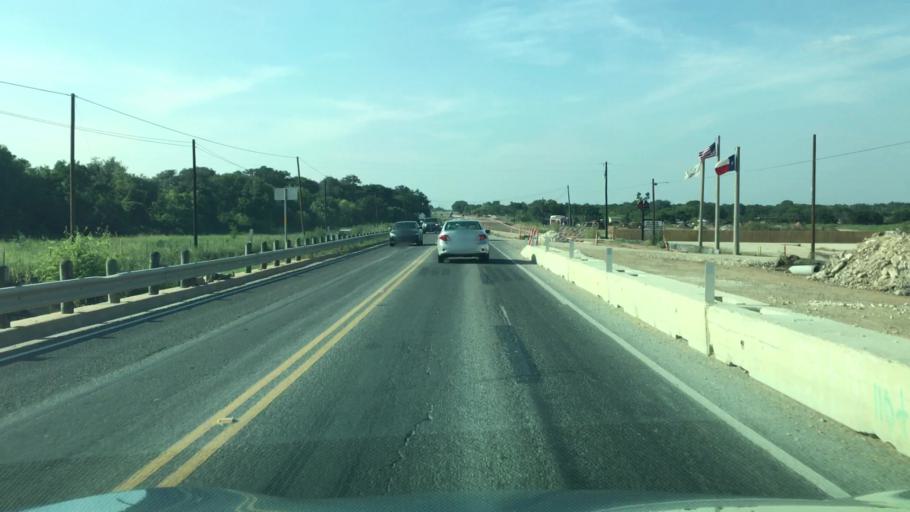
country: US
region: Texas
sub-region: Hays County
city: Buda
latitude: 30.0697
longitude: -97.8742
